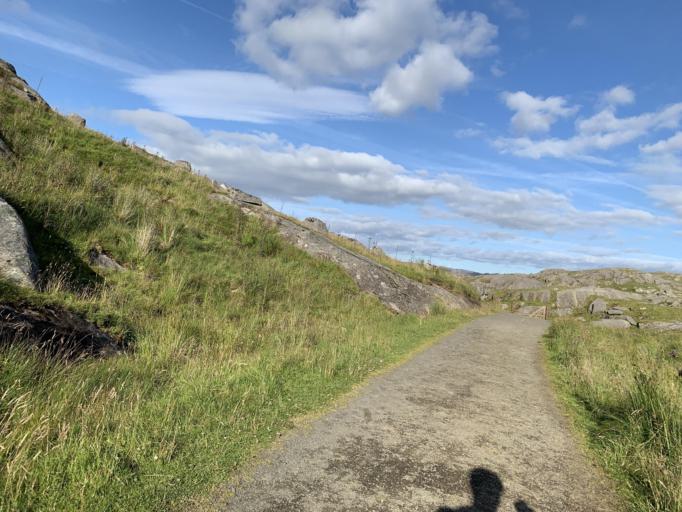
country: NO
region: Rogaland
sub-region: Eigersund
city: Egersund
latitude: 58.4417
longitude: 5.8821
